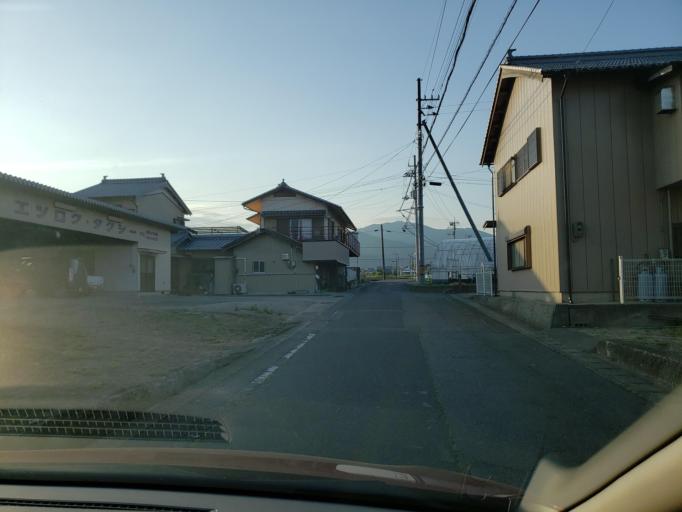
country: JP
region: Tokushima
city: Wakimachi
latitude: 34.0820
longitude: 134.2338
